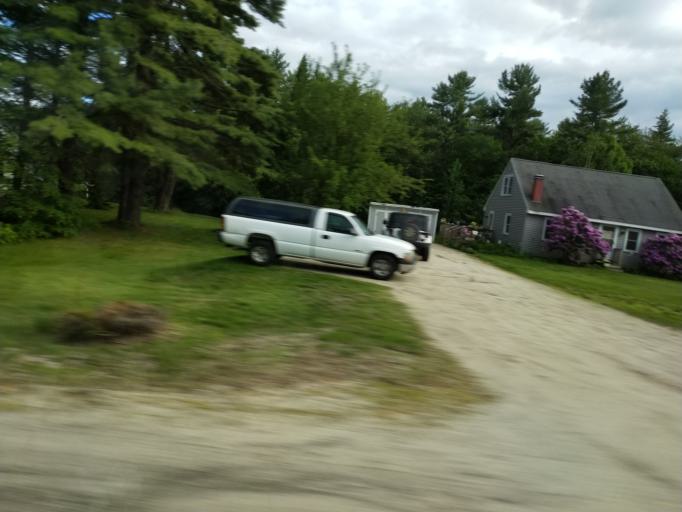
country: US
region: Maine
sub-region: Cumberland County
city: New Gloucester
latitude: 43.8860
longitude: -70.3163
